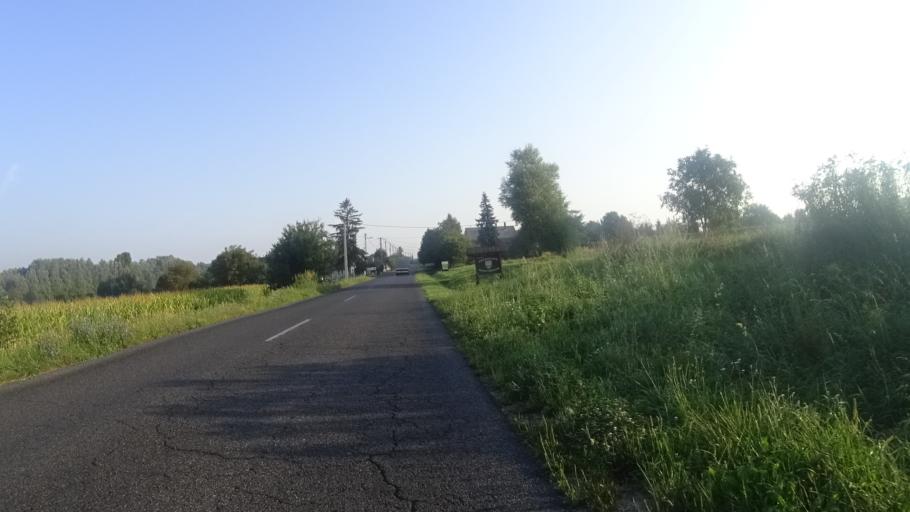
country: HU
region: Zala
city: Zalakomar
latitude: 46.5854
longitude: 17.1768
